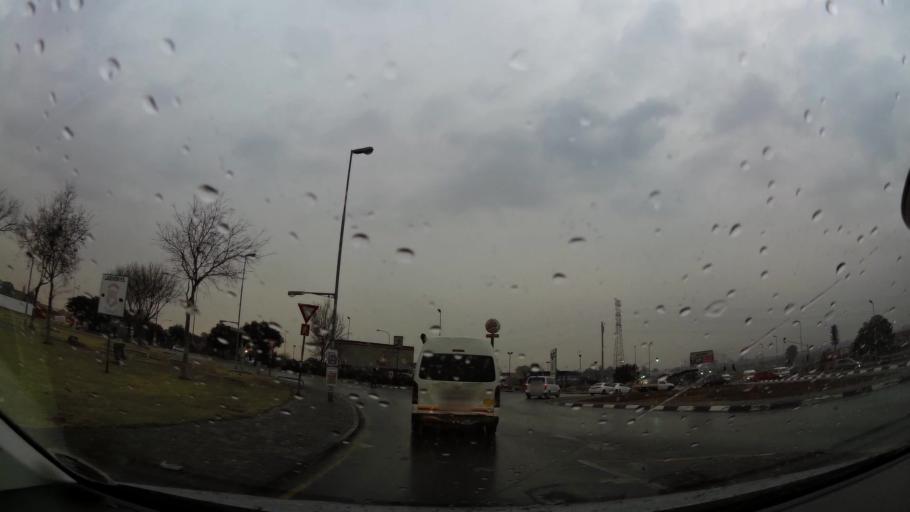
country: ZA
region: Gauteng
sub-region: City of Johannesburg Metropolitan Municipality
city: Soweto
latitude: -26.2630
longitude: 27.8846
